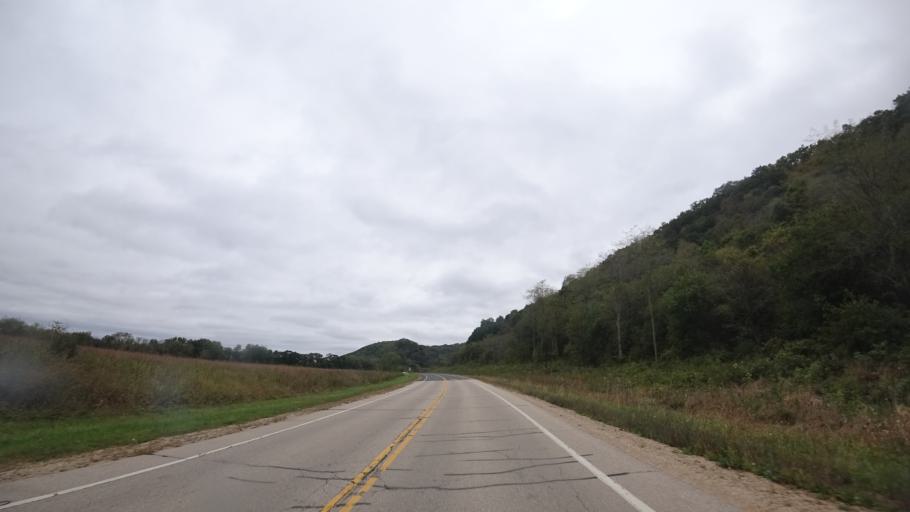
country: US
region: Wisconsin
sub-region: Grant County
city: Boscobel
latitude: 43.2050
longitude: -90.6430
